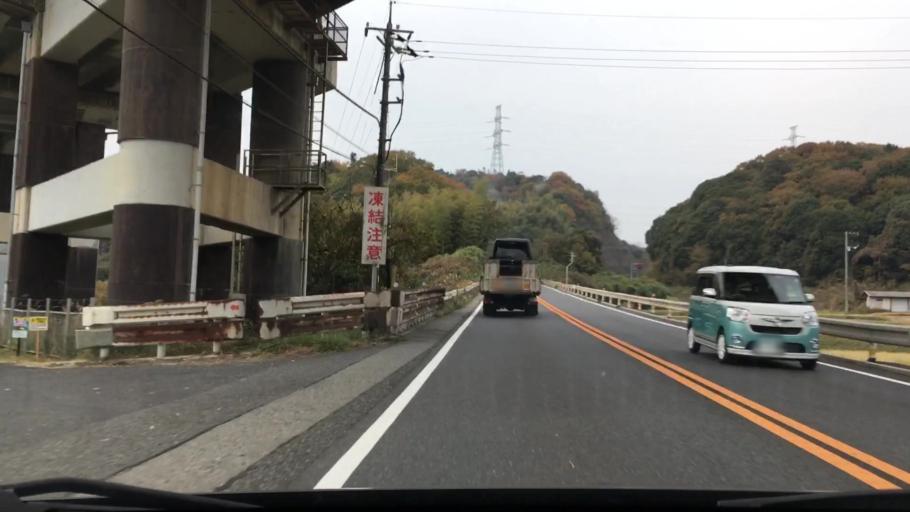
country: JP
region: Yamaguchi
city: Onoda
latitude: 34.0371
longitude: 131.2509
